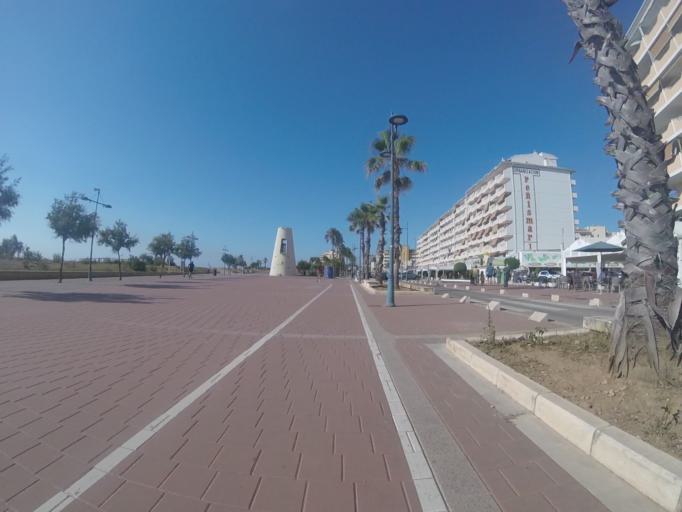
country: ES
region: Valencia
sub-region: Provincia de Castello
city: Peniscola
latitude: 40.3844
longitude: 0.4093
